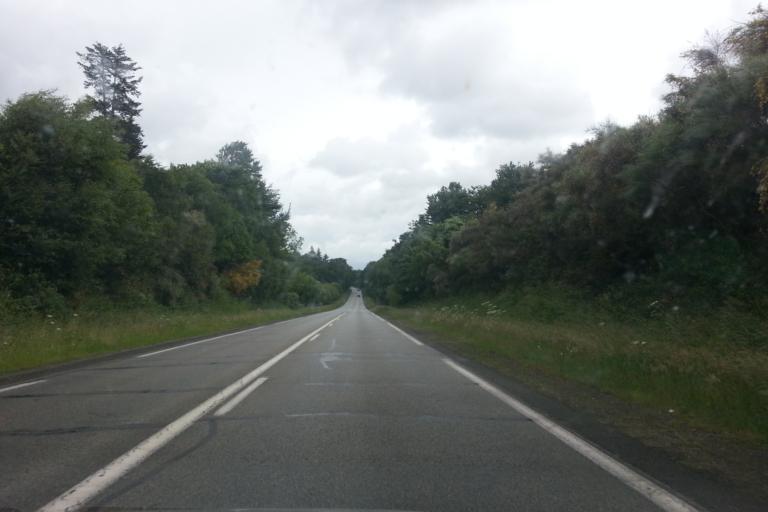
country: FR
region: Brittany
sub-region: Departement du Morbihan
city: Caudan
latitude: 47.8011
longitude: -3.3384
